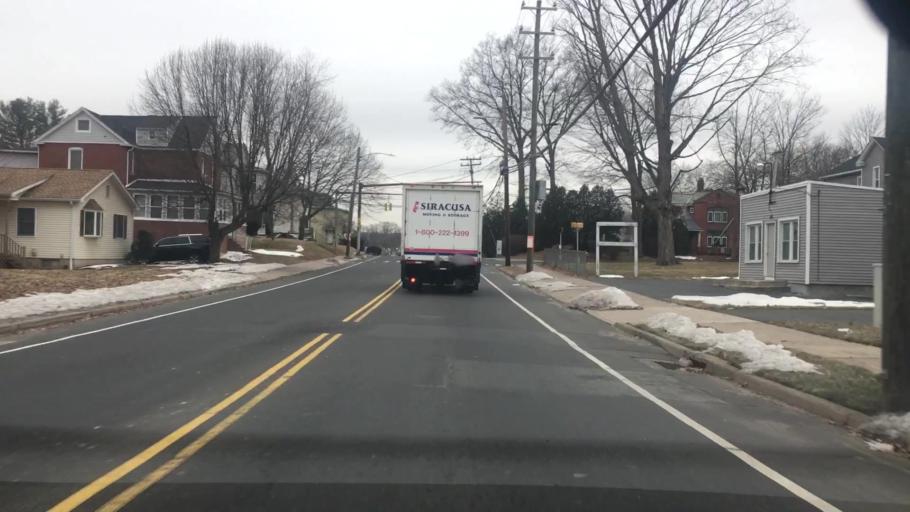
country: US
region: Connecticut
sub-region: Hartford County
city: Kensington
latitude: 41.6537
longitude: -72.7577
